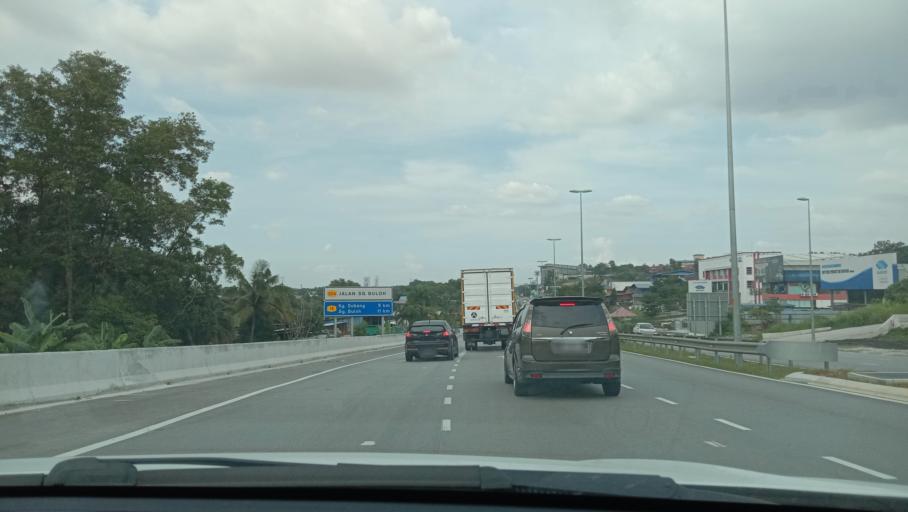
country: MY
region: Selangor
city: Kampung Baru Subang
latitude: 3.1287
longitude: 101.5259
